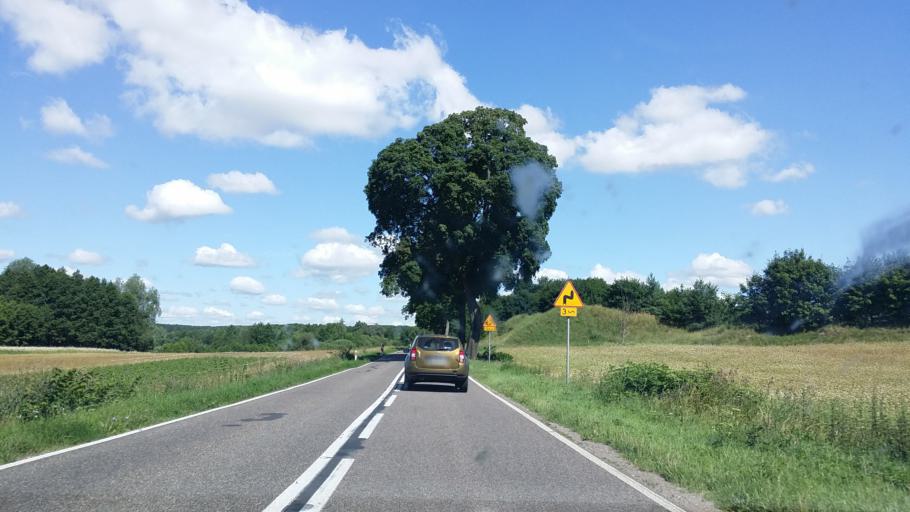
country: PL
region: West Pomeranian Voivodeship
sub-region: Powiat drawski
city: Drawsko Pomorskie
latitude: 53.4928
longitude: 15.8001
